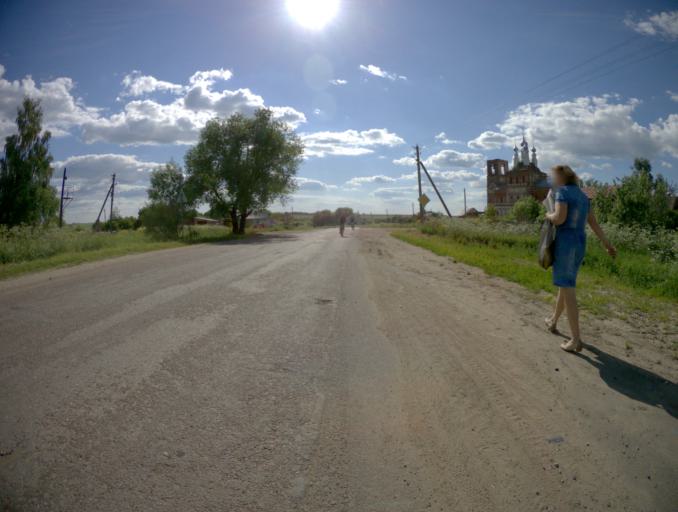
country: RU
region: Vladimir
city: Suzdal'
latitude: 56.3430
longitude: 40.3311
